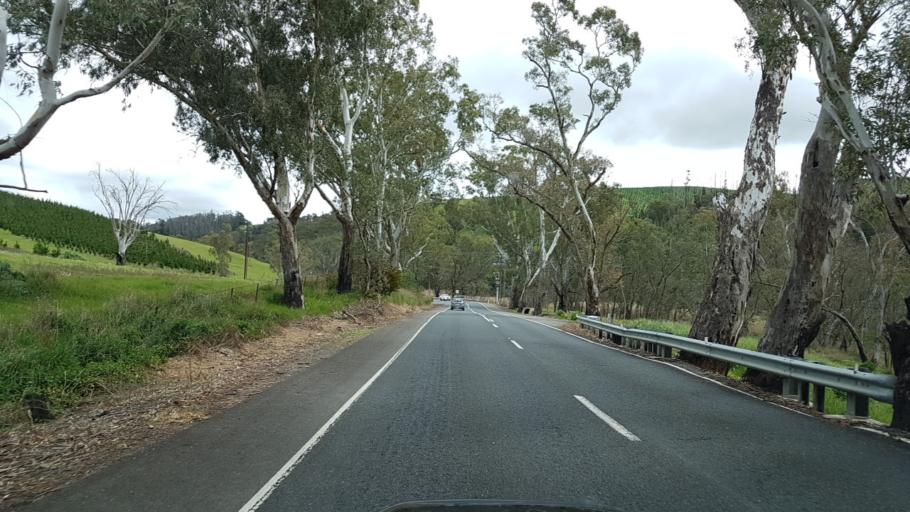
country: AU
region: South Australia
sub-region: Adelaide Hills
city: Gumeracha
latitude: -34.8201
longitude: 138.8594
